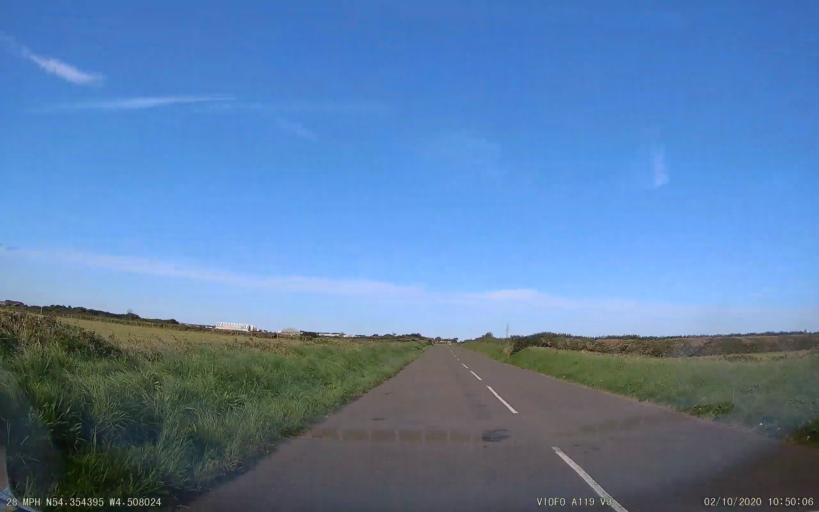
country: IM
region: Ramsey
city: Ramsey
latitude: 54.3544
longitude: -4.5081
